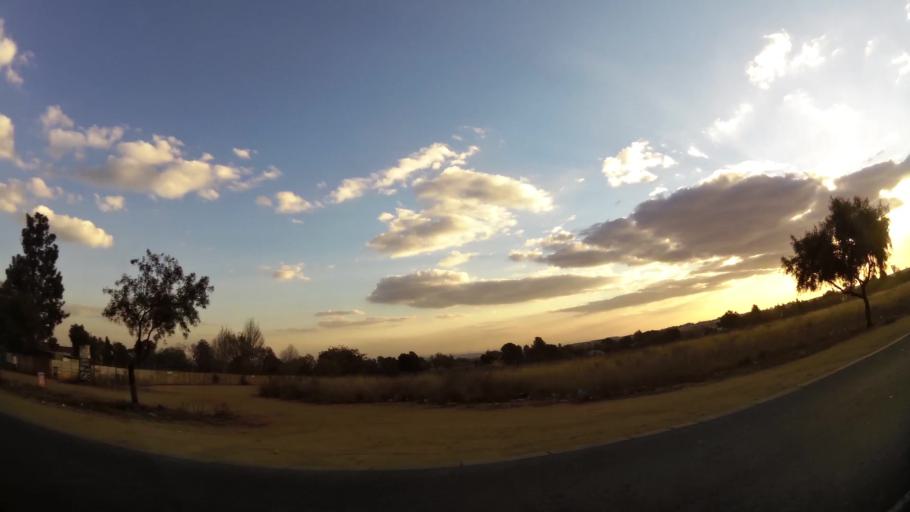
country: ZA
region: Gauteng
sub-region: City of Johannesburg Metropolitan Municipality
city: Midrand
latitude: -26.0056
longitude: 28.1583
